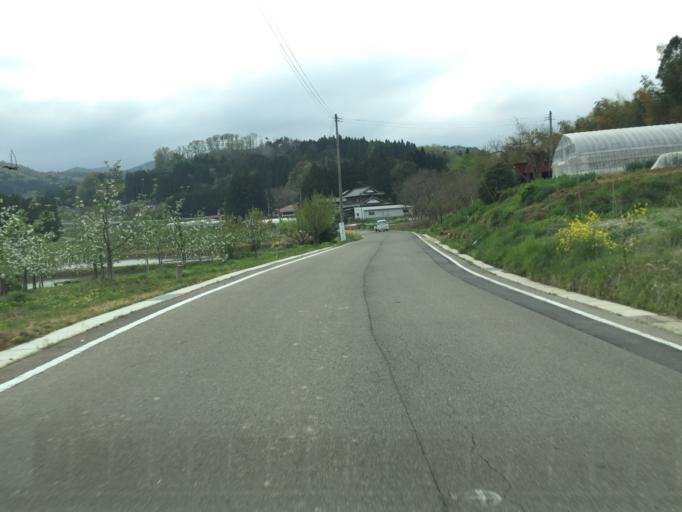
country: JP
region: Fukushima
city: Nihommatsu
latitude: 37.6496
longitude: 140.4282
